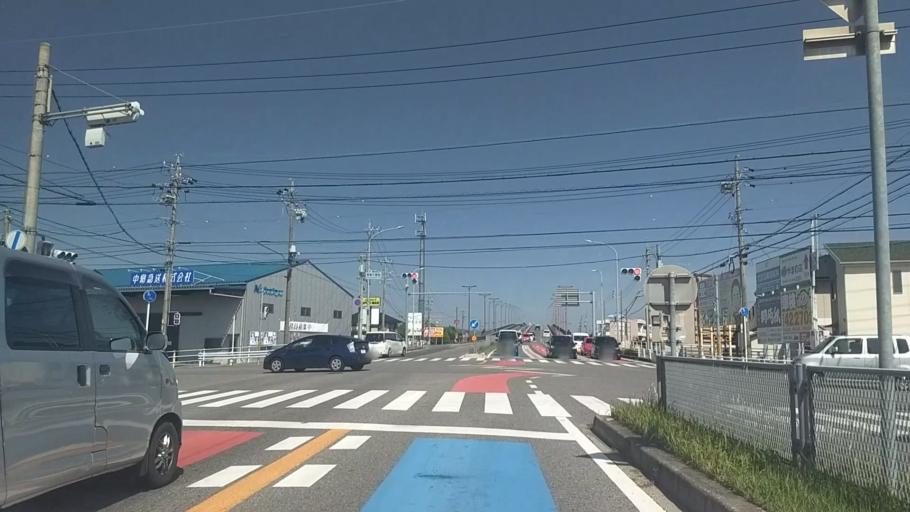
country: JP
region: Aichi
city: Okazaki
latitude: 34.9839
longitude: 137.1393
